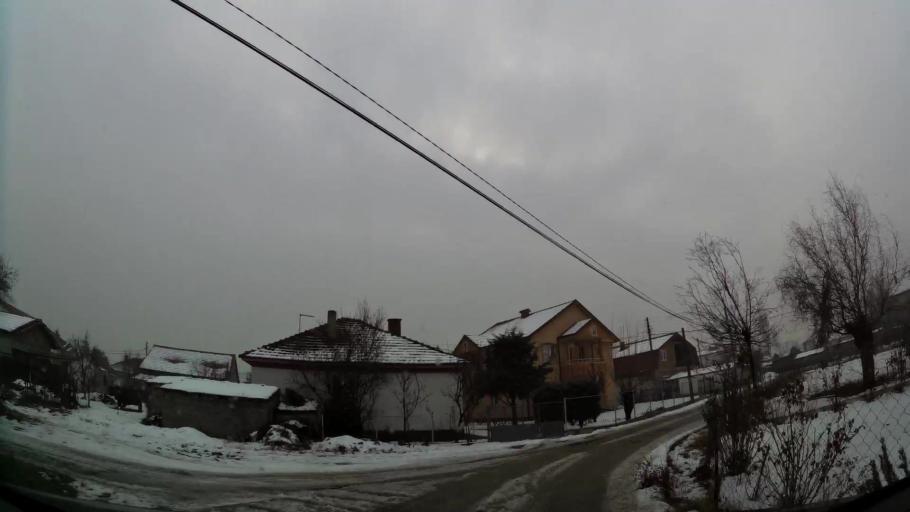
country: MK
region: Petrovec
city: Petrovec
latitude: 41.9407
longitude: 21.6143
